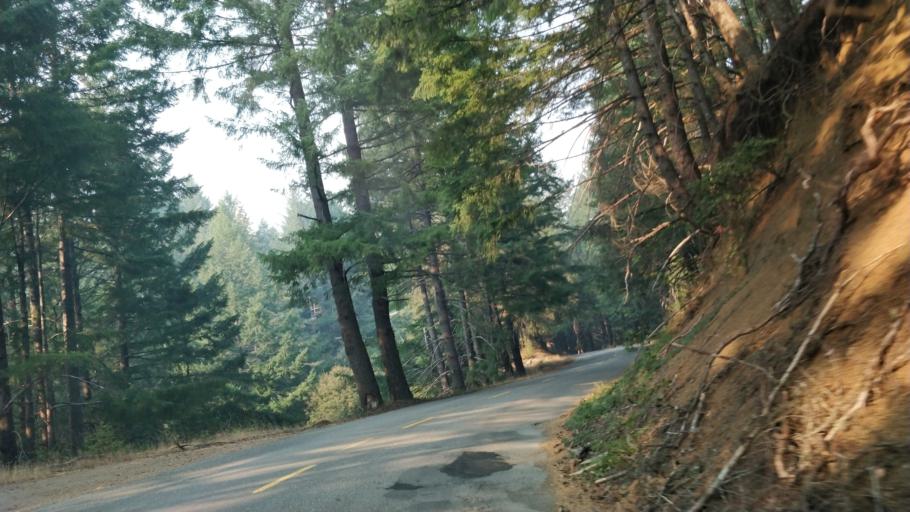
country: US
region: California
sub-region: Humboldt County
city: Rio Dell
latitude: 40.2880
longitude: -124.0568
